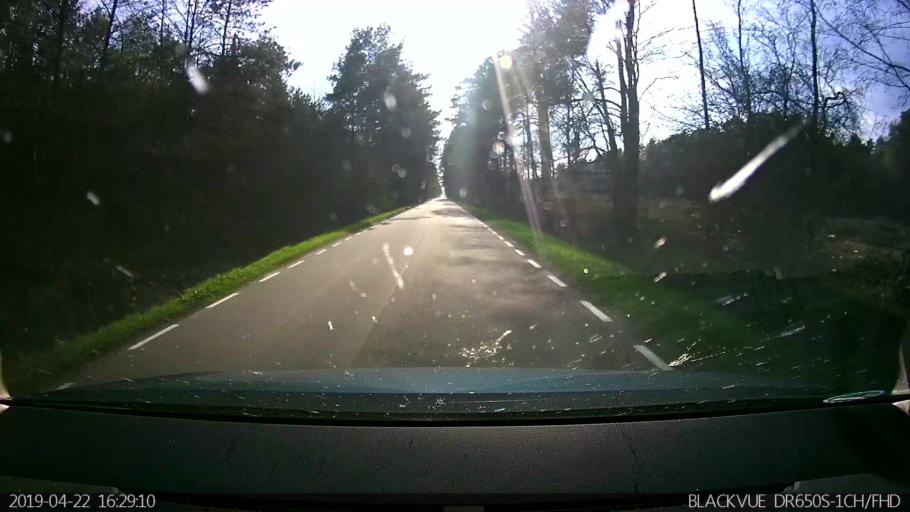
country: PL
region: Podlasie
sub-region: Powiat siemiatycki
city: Milejczyce
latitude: 52.5372
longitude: 23.1699
